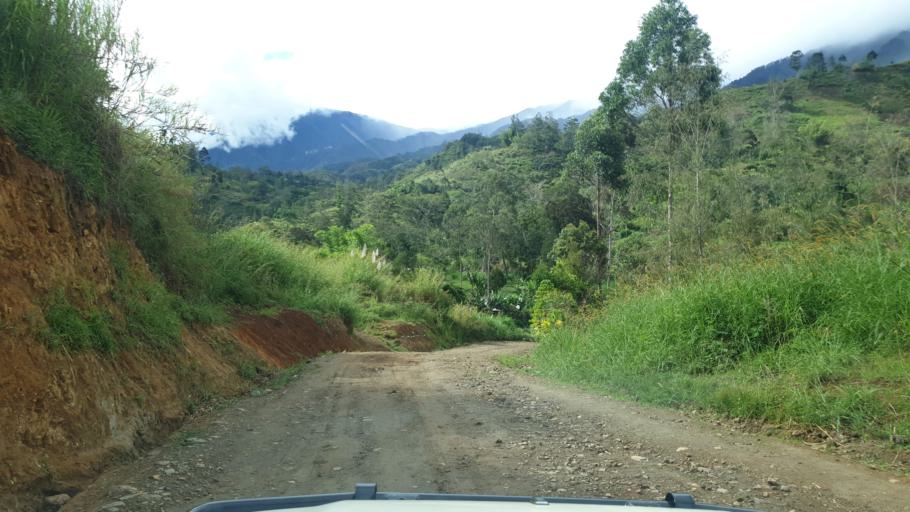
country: PG
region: Eastern Highlands
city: Goroka
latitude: -5.9364
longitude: 145.2668
